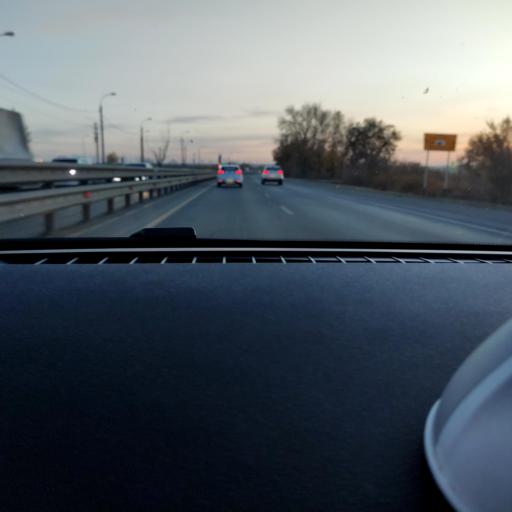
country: RU
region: Samara
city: Samara
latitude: 53.0982
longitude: 50.1587
